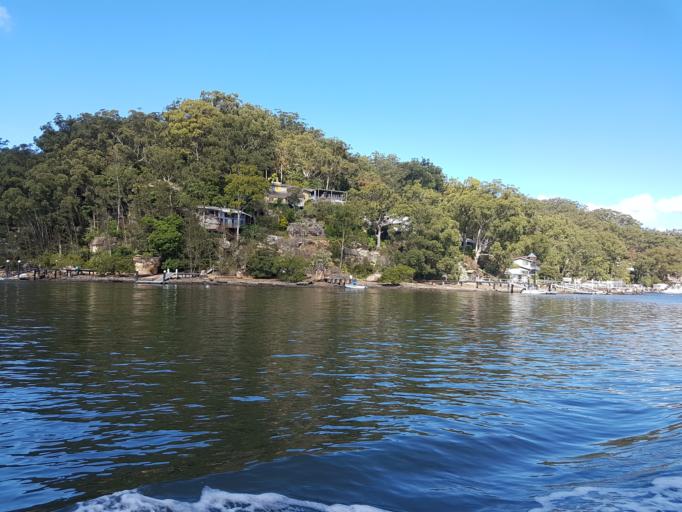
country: AU
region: New South Wales
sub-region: Gosford Shire
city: Umina
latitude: -33.5361
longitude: 151.2359
